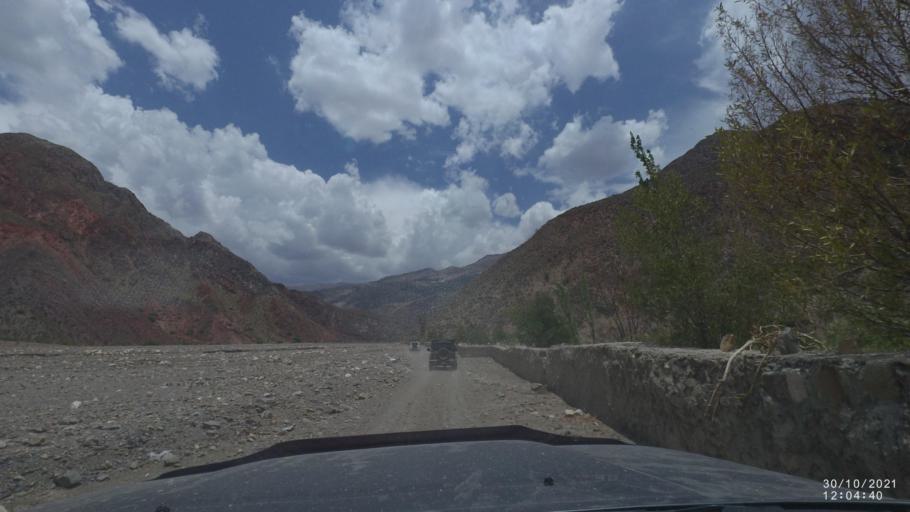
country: BO
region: Cochabamba
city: Colchani
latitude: -17.5319
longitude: -66.6197
